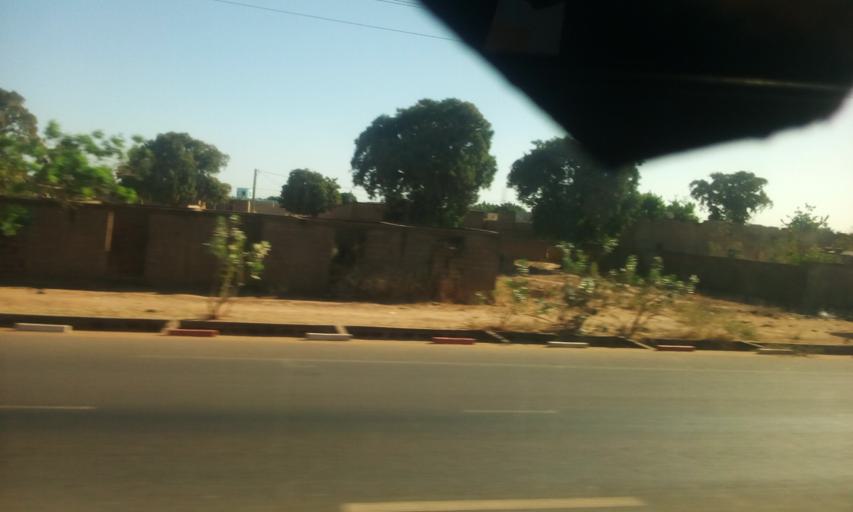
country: ML
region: Segou
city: Segou
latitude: 13.4188
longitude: -6.3039
